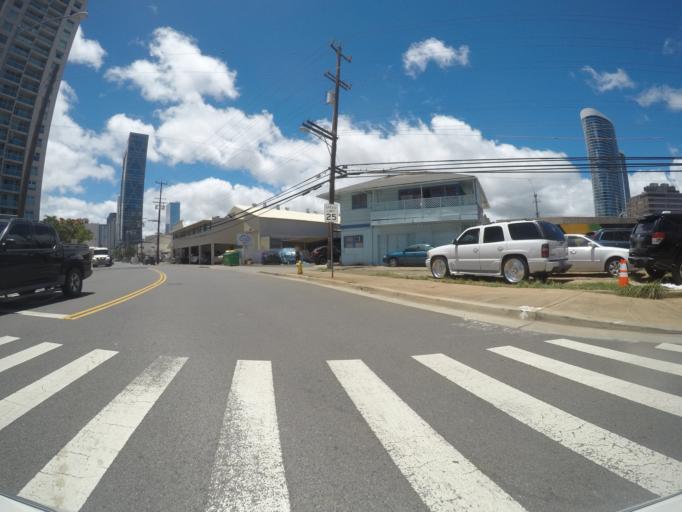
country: US
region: Hawaii
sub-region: Honolulu County
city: Honolulu
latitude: 21.2942
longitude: -157.8497
